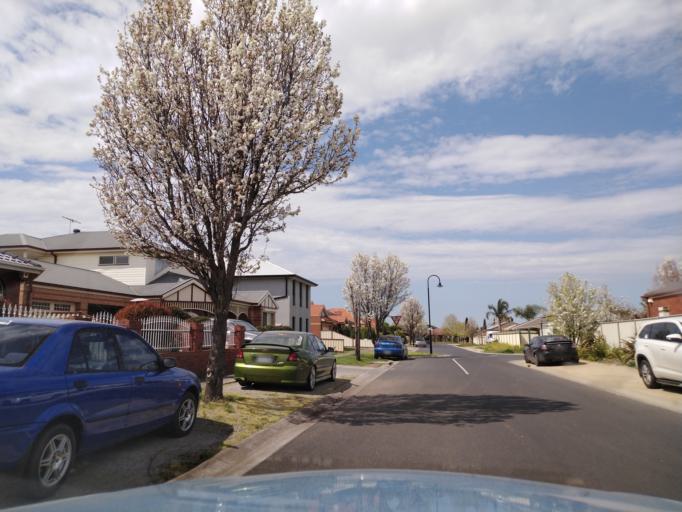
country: AU
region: Victoria
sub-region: Wyndham
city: Hoppers Crossing
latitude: -37.8495
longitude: 144.7083
